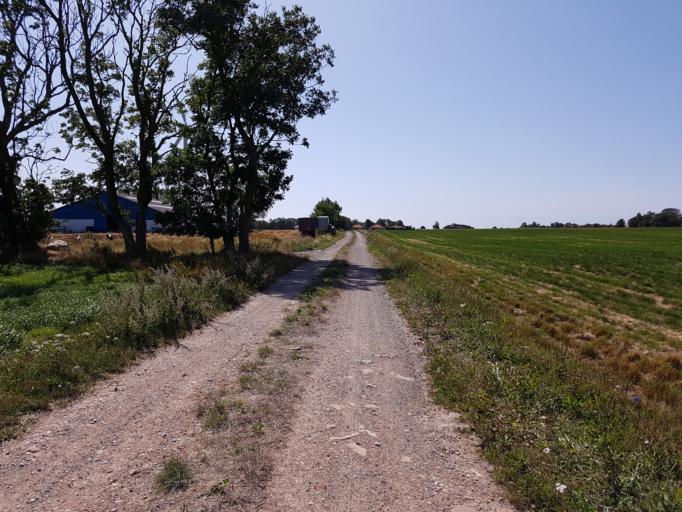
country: DK
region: Zealand
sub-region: Guldborgsund Kommune
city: Nykobing Falster
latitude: 54.5946
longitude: 11.9373
